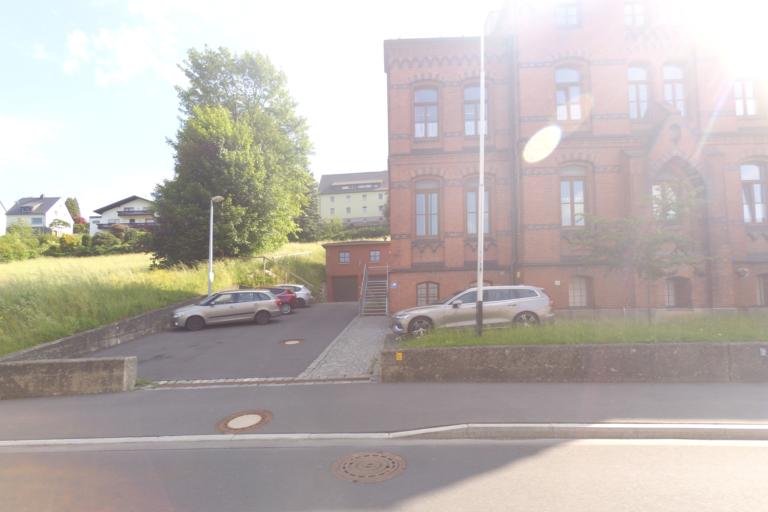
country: DE
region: Bavaria
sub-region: Upper Franconia
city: Ludwigsstadt
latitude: 50.4884
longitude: 11.3853
